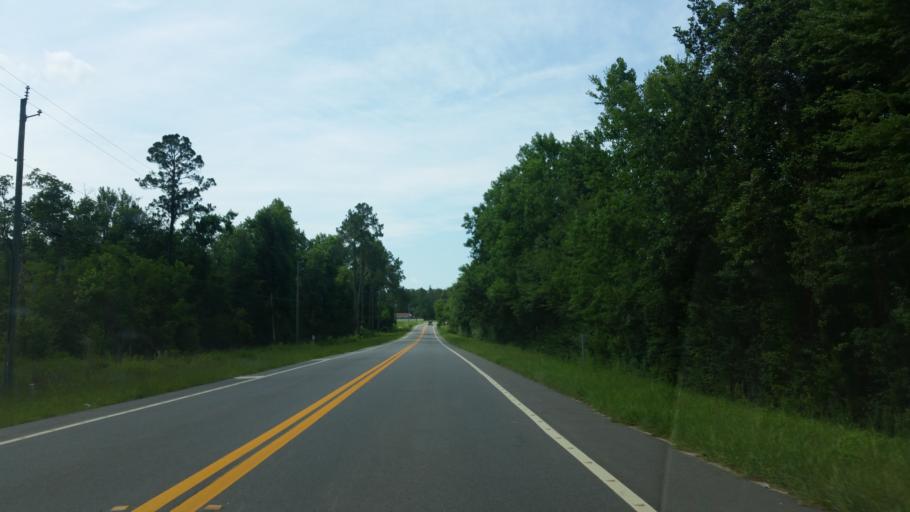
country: US
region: Florida
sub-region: Escambia County
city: Cantonment
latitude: 30.6387
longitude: -87.3844
